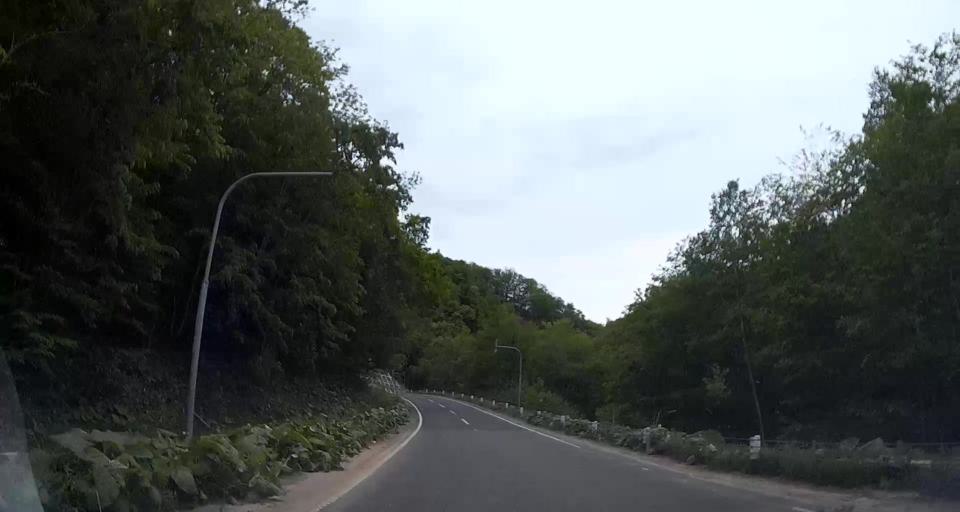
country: JP
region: Hokkaido
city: Chitose
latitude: 42.7895
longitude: 142.0510
